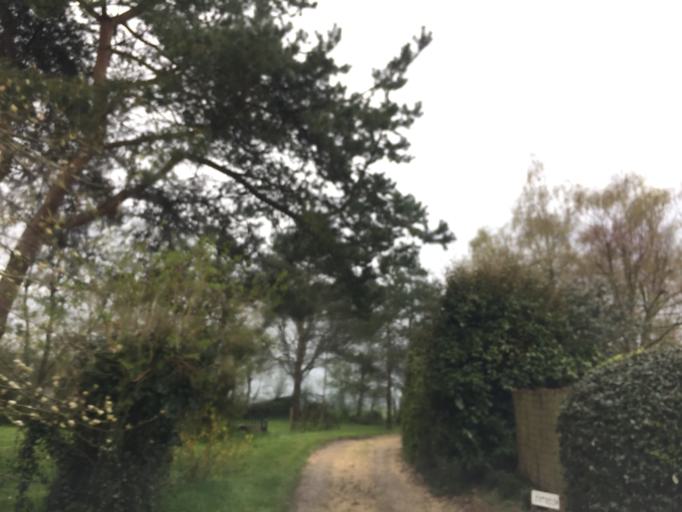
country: FR
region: Pays de la Loire
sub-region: Departement de la Loire-Atlantique
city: Soudan
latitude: 47.7545
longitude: -1.2903
